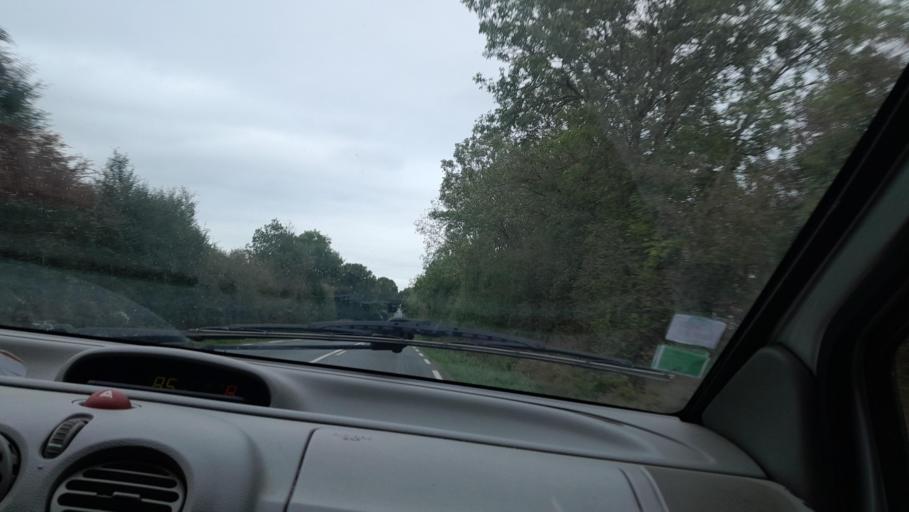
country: FR
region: Pays de la Loire
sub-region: Departement de Maine-et-Loire
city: Pouance
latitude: 47.6561
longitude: -1.1977
